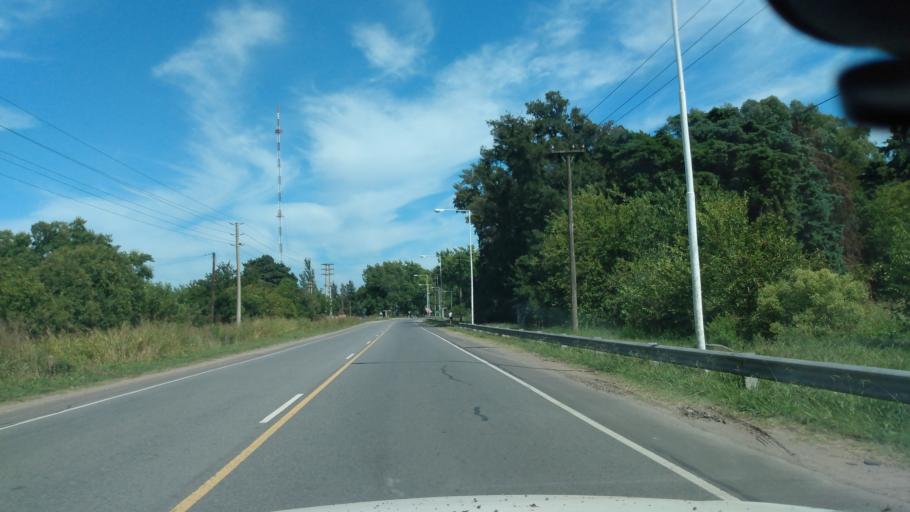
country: AR
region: Buenos Aires
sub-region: Partido de Lujan
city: Lujan
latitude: -34.5489
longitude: -59.1462
